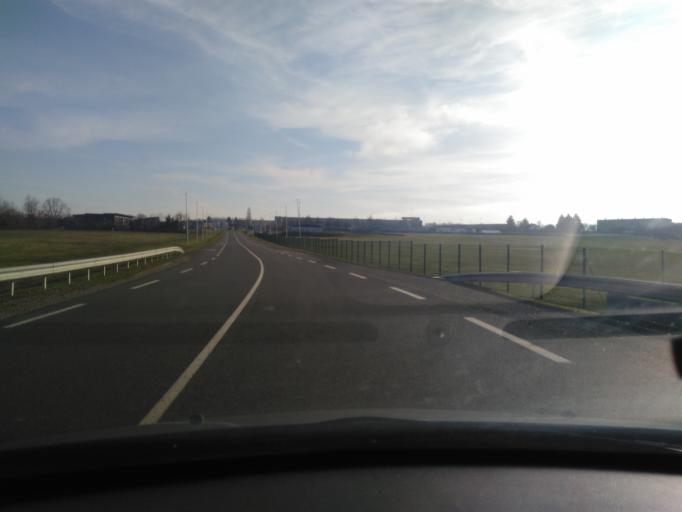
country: FR
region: Bourgogne
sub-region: Departement de la Nievre
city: Magny-Cours
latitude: 46.8697
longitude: 3.1555
